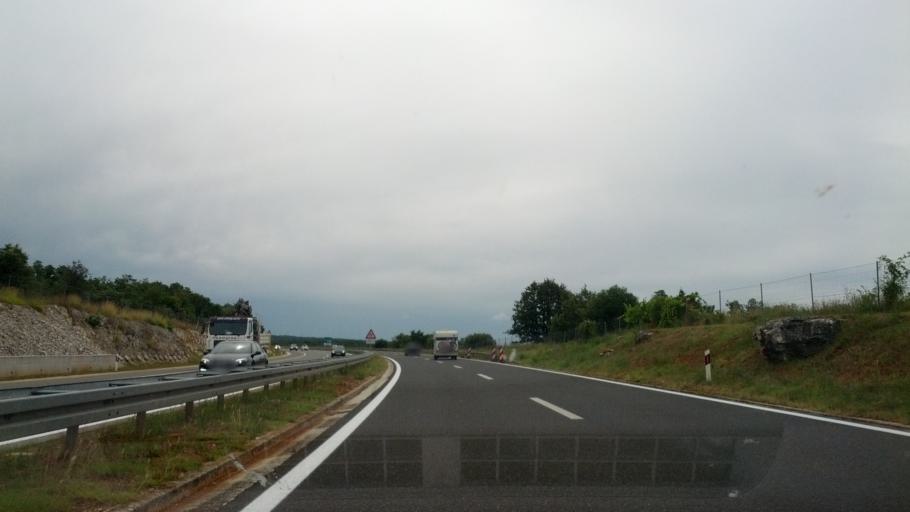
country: HR
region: Istarska
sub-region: Grad Rovinj
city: Rovinj
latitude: 45.1274
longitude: 13.7737
